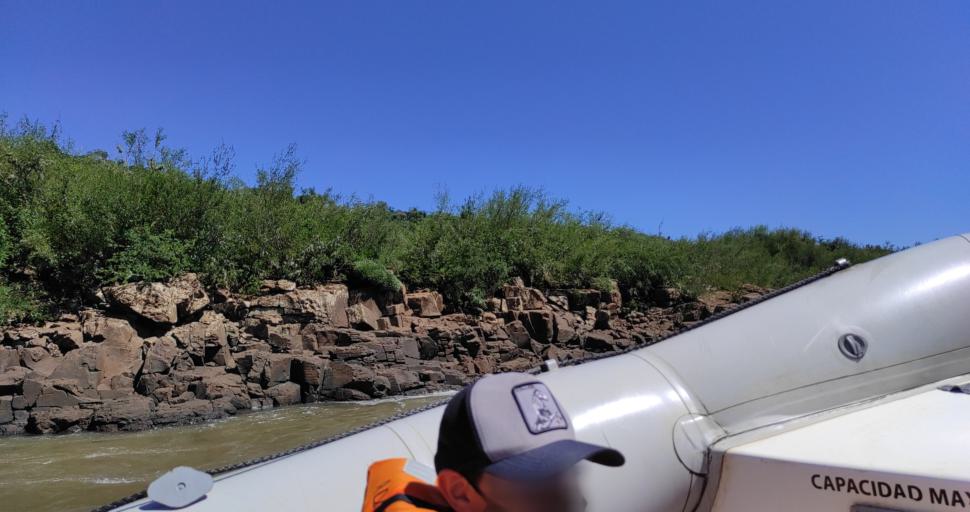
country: BR
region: Rio Grande do Sul
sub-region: Tres Passos
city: Tres Passos
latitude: -27.1547
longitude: -53.8892
